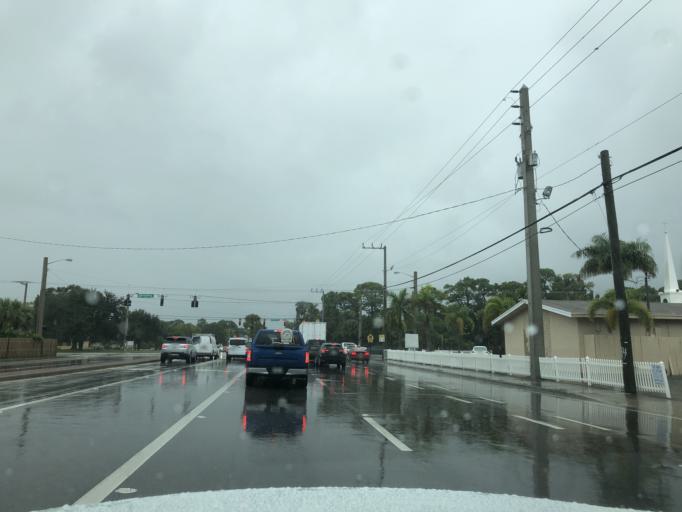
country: US
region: Florida
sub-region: Palm Beach County
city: Haverhill
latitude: 26.6914
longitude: -80.1198
